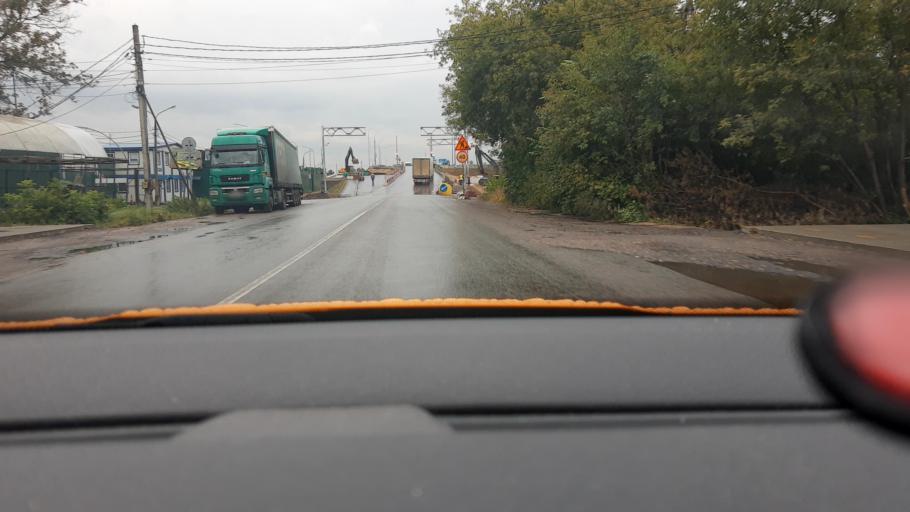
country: RU
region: Moskovskaya
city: Obukhovo
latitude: 55.8257
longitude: 38.2626
